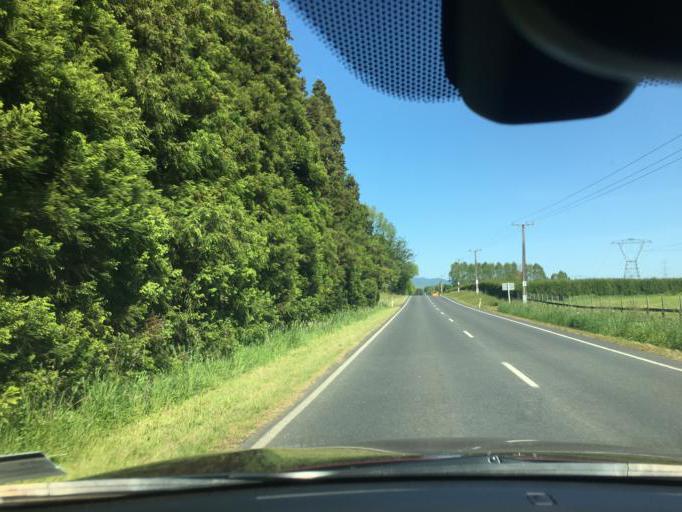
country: NZ
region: Waikato
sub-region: Waipa District
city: Cambridge
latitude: -37.9083
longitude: 175.4530
